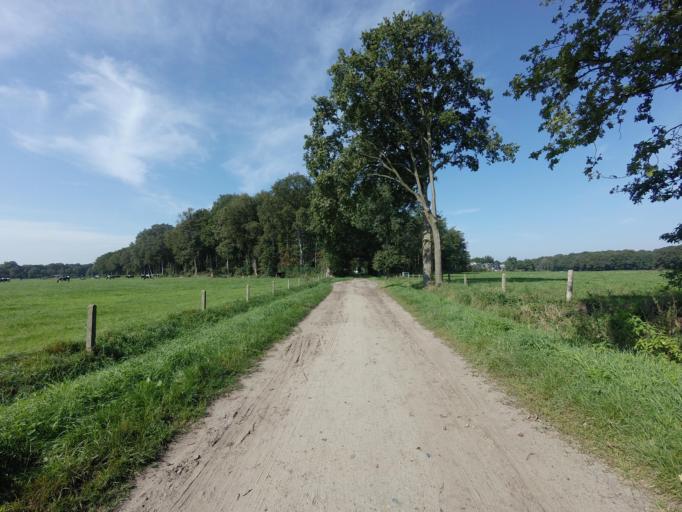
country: NL
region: Overijssel
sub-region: Gemeente Enschede
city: Enschede
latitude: 52.1887
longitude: 6.9138
